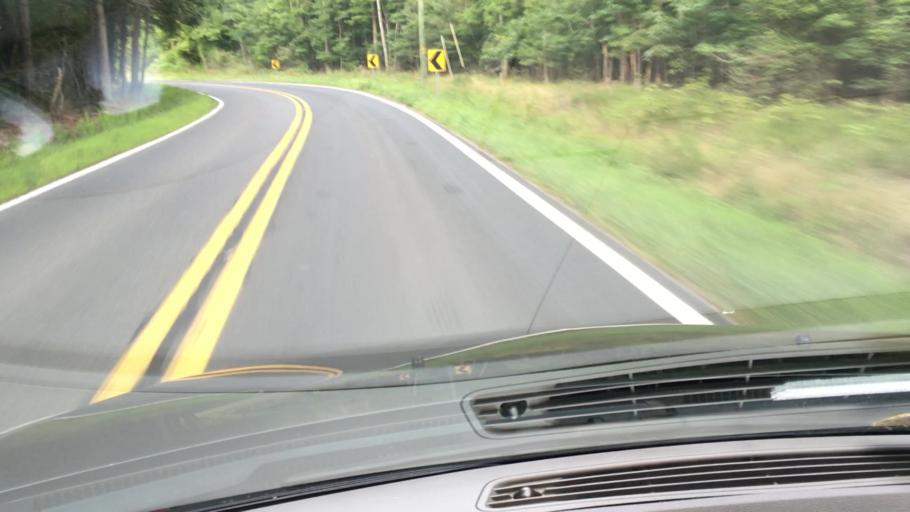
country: US
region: Delaware
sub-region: Sussex County
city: Ocean View
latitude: 38.5077
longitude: -75.1143
